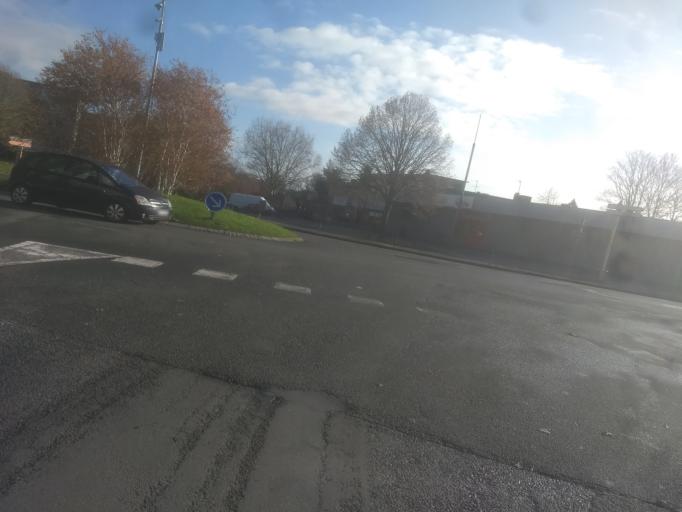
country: FR
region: Nord-Pas-de-Calais
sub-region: Departement du Pas-de-Calais
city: Anzin-Saint-Aubin
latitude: 50.3010
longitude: 2.7459
